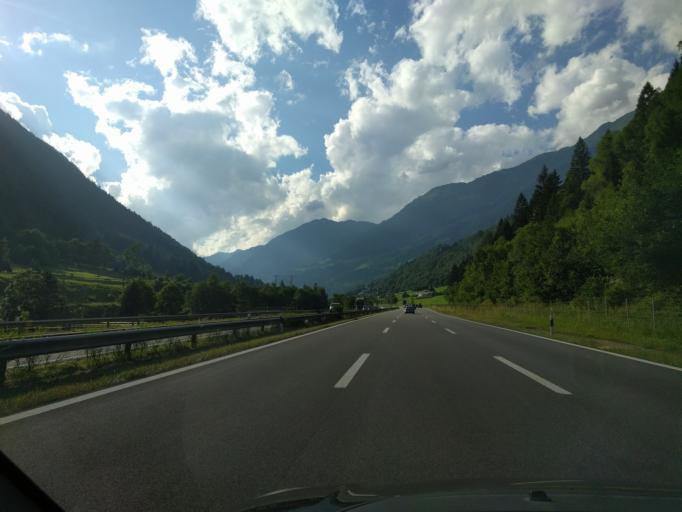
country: CH
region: Ticino
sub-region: Leventina District
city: Faido
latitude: 46.4945
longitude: 8.7367
